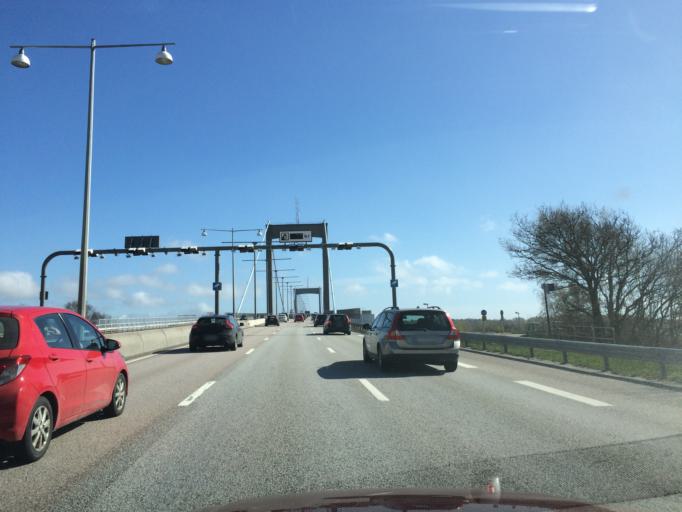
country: SE
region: Vaestra Goetaland
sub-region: Goteborg
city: Majorna
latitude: 57.6952
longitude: 11.8988
